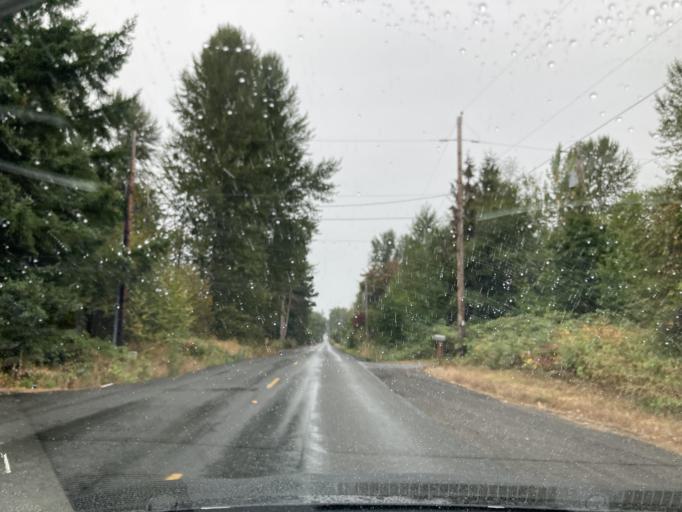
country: US
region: Washington
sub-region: Pierce County
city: Graham
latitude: 47.0519
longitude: -122.2870
